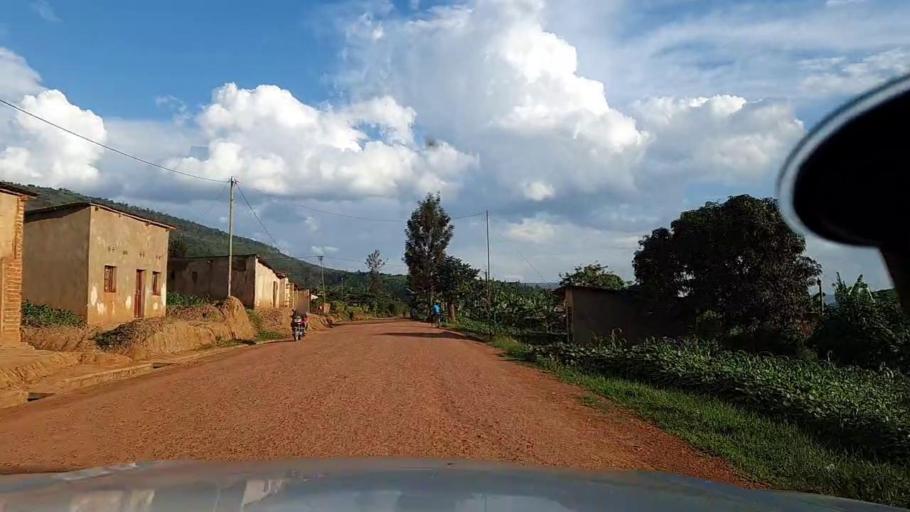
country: RW
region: Kigali
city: Kigali
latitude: -1.9131
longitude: 29.9849
